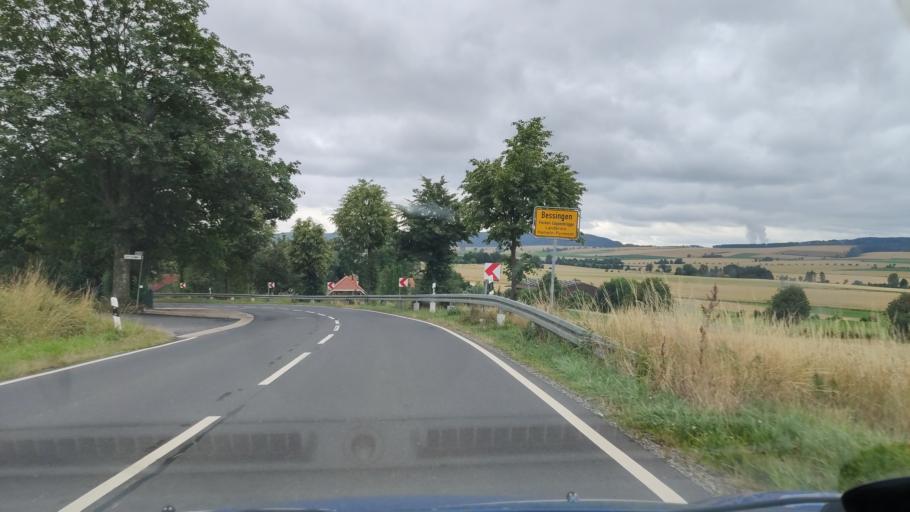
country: DE
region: Lower Saxony
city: Coppenbrugge
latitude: 52.1064
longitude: 9.5001
